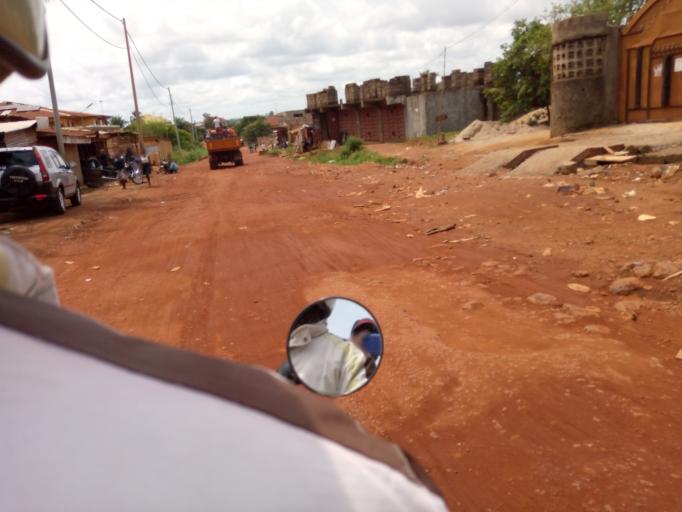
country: SL
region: Western Area
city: Waterloo
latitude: 8.3590
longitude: -13.0803
